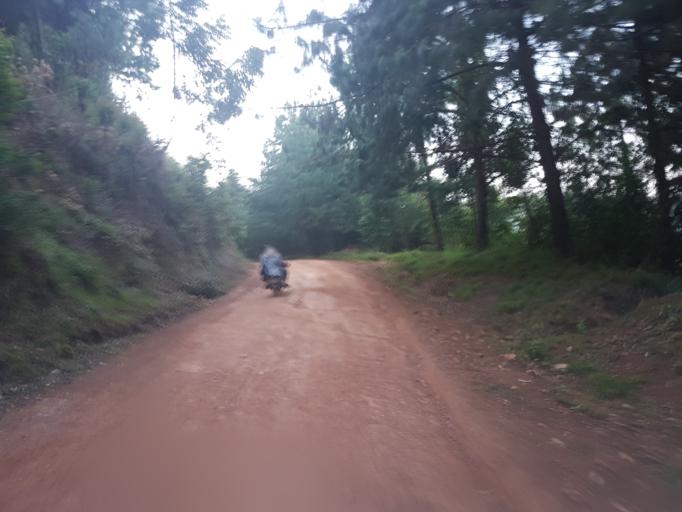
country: UG
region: Western Region
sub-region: Kanungu District
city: Kanungu
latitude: -1.0471
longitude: 29.8828
